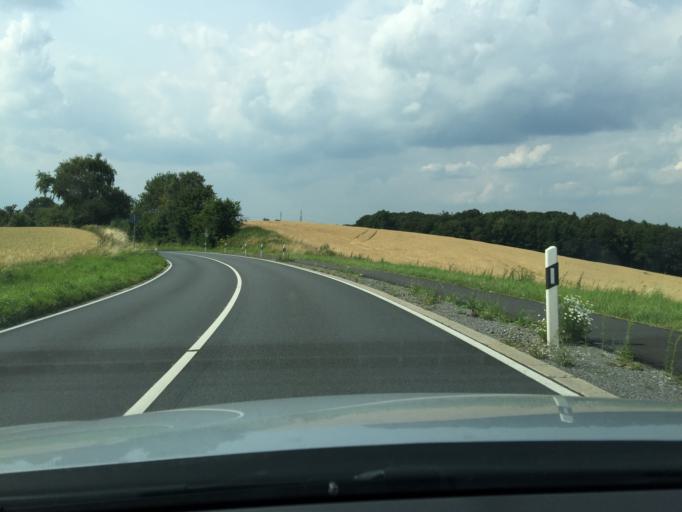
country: DE
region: North Rhine-Westphalia
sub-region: Regierungsbezirk Dusseldorf
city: Velbert
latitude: 51.3574
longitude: 7.0837
